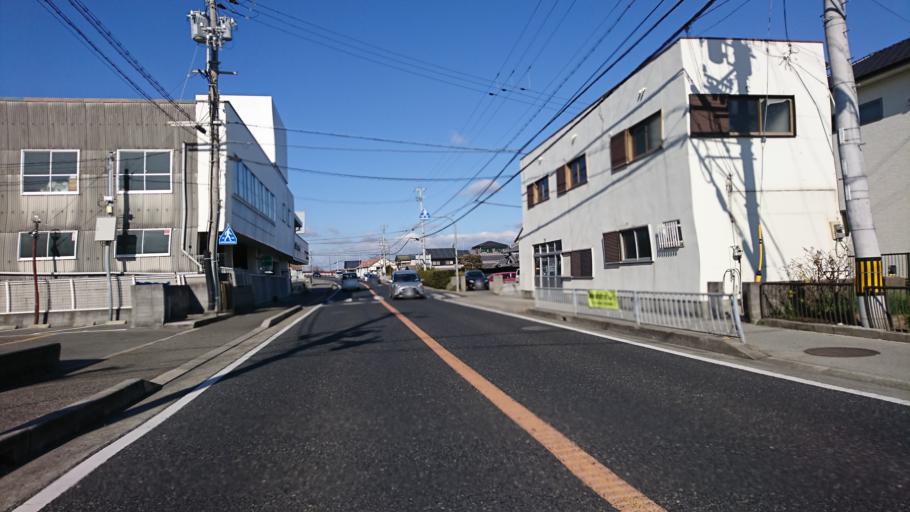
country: JP
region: Hyogo
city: Kakogawacho-honmachi
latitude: 34.7262
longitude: 134.8871
